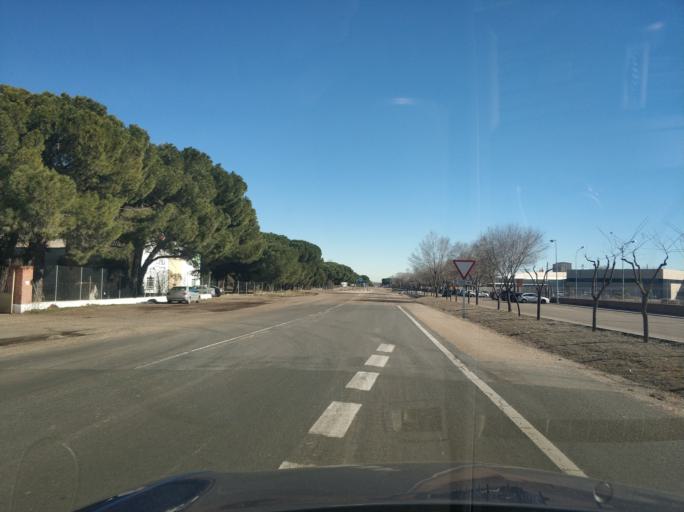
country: ES
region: Castille and Leon
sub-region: Provincia de Valladolid
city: Tordesillas
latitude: 41.4902
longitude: -5.0199
